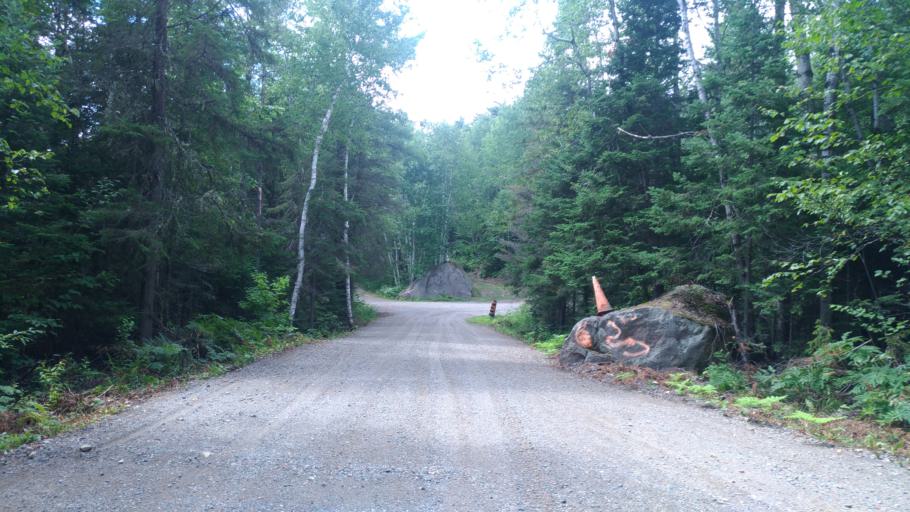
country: CA
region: Ontario
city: Rayside-Balfour
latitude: 46.5874
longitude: -81.5453
